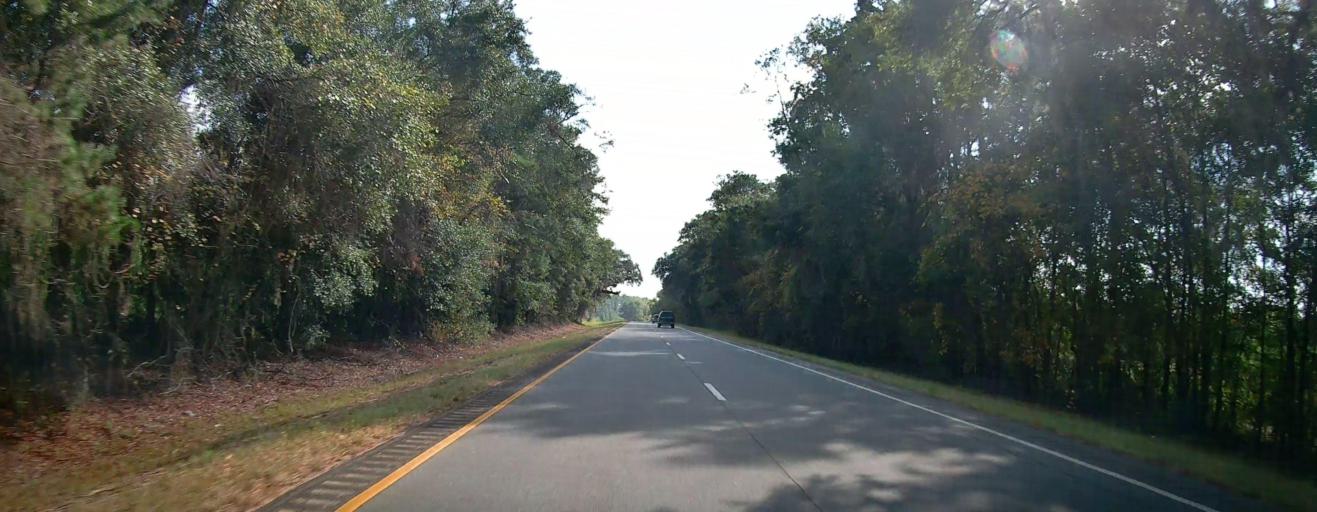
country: US
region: Georgia
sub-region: Grady County
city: Cairo
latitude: 30.6923
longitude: -84.1497
